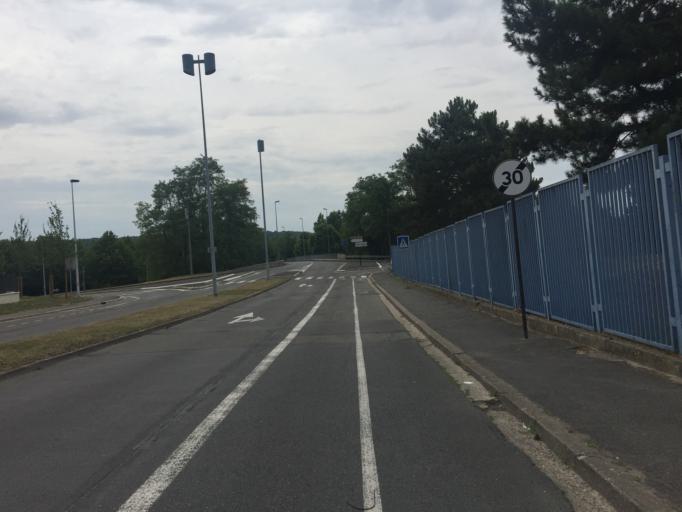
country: FR
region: Ile-de-France
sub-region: Departement de Seine-et-Marne
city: Nanteuil-les-Meaux
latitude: 48.9479
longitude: 2.9104
